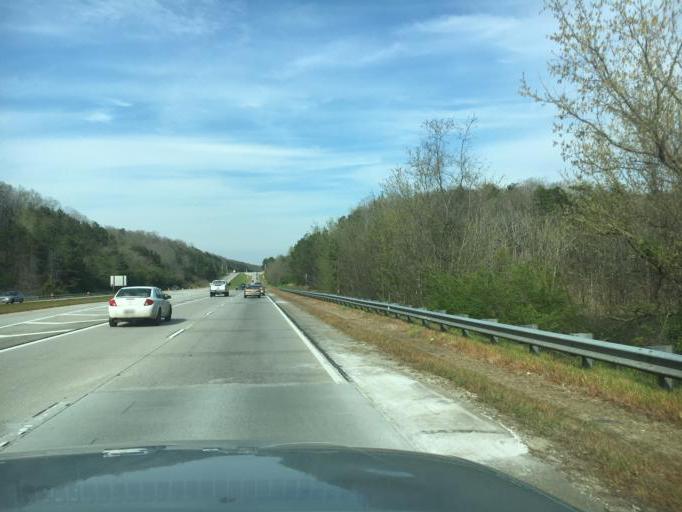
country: US
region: Georgia
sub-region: Hall County
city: Gainesville
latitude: 34.3354
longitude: -83.7787
